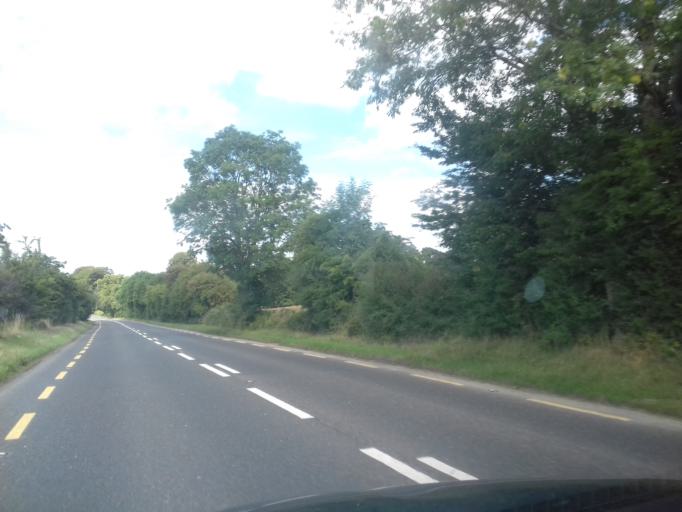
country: IE
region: Leinster
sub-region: Wicklow
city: Valleymount
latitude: 53.0585
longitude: -6.6254
